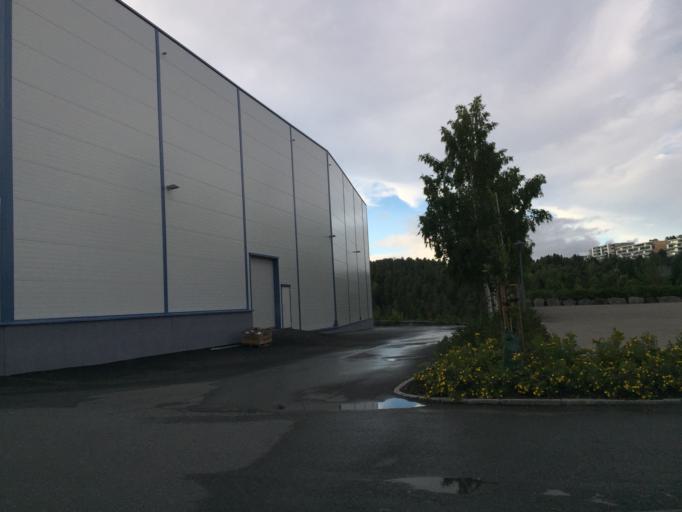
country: NO
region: Akershus
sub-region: Oppegard
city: Kolbotn
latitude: 59.8411
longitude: 10.8206
